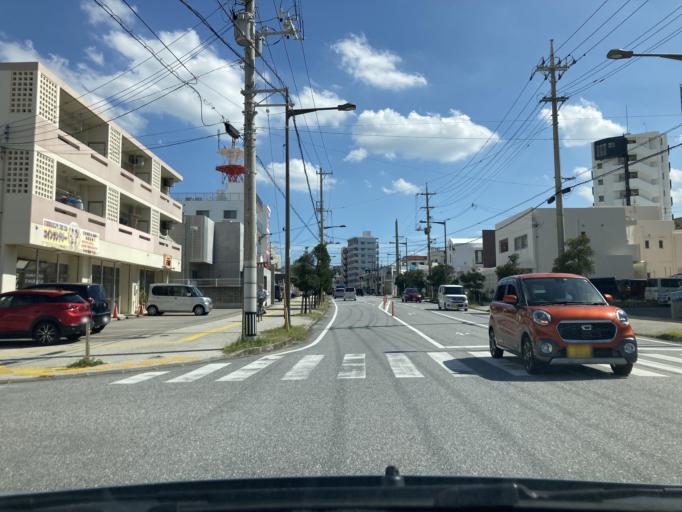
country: JP
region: Okinawa
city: Ginowan
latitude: 26.2699
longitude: 127.7320
